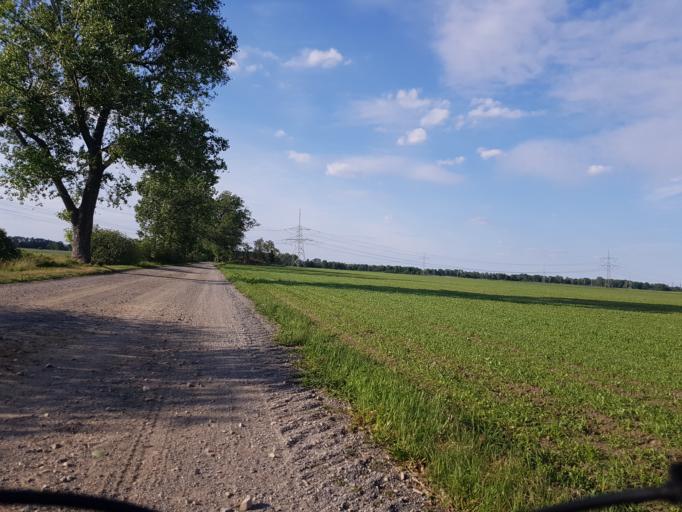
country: DE
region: Brandenburg
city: Merzdorf
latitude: 51.4214
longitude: 13.5266
